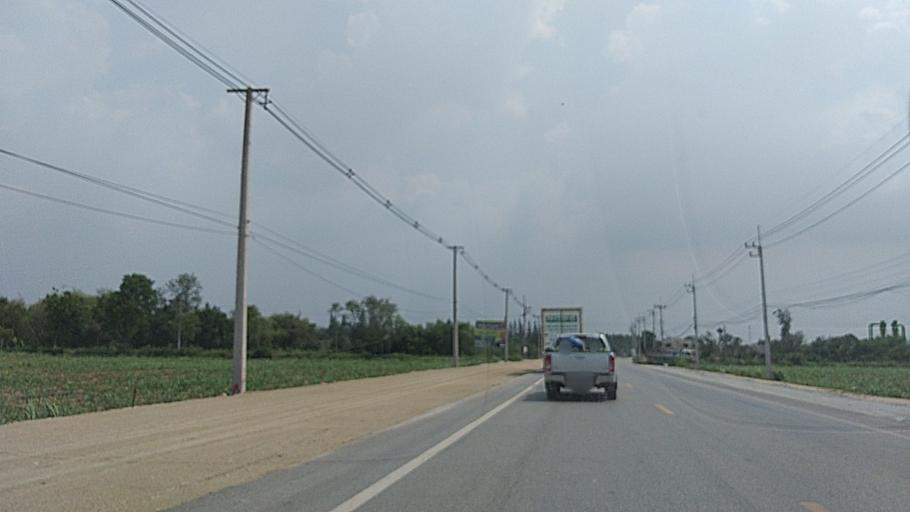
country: TH
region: Chon Buri
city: Phanat Nikhom
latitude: 13.3654
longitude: 101.1962
